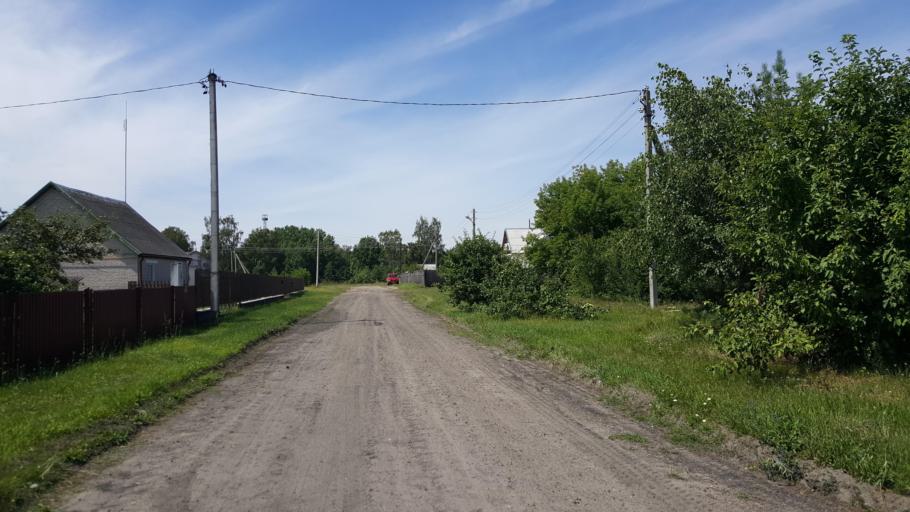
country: BY
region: Brest
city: Pruzhany
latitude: 52.5673
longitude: 24.2152
